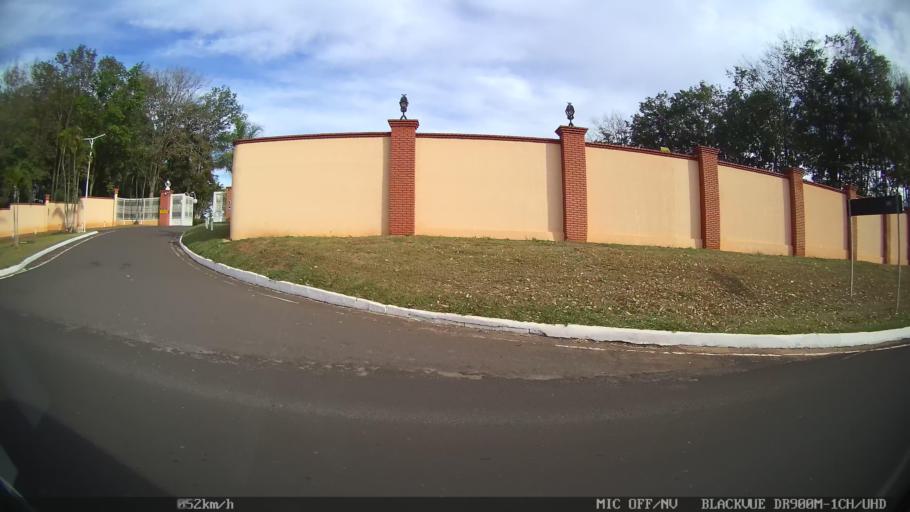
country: BR
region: Sao Paulo
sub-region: Catanduva
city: Catanduva
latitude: -21.1113
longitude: -48.9623
